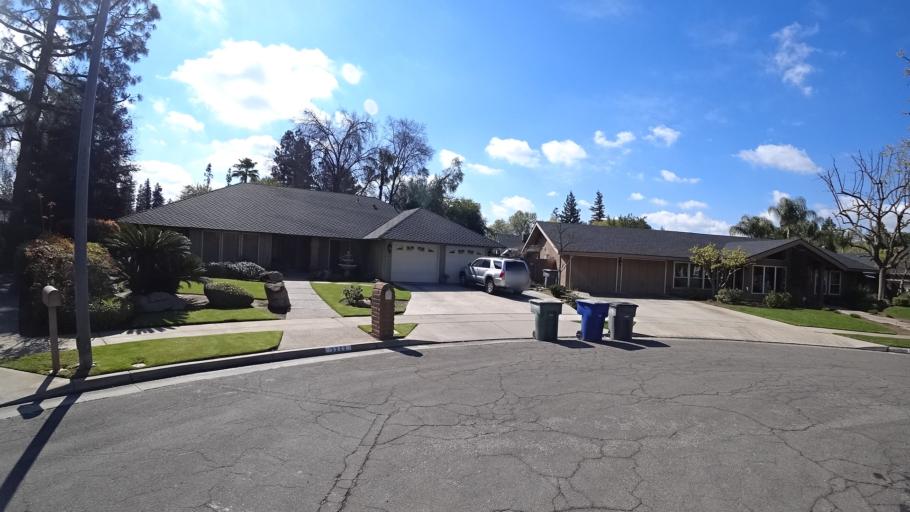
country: US
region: California
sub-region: Fresno County
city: Fresno
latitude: 36.8316
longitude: -119.8493
